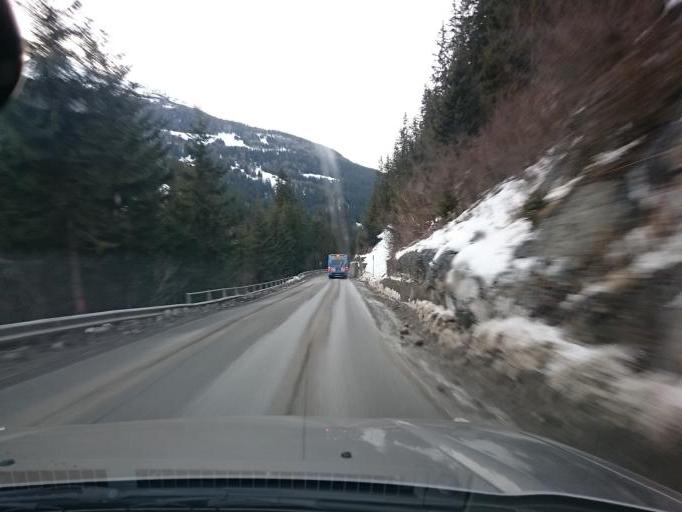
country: IT
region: Lombardy
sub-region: Provincia di Sondrio
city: Sant'Antonio
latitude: 46.4241
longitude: 10.4670
